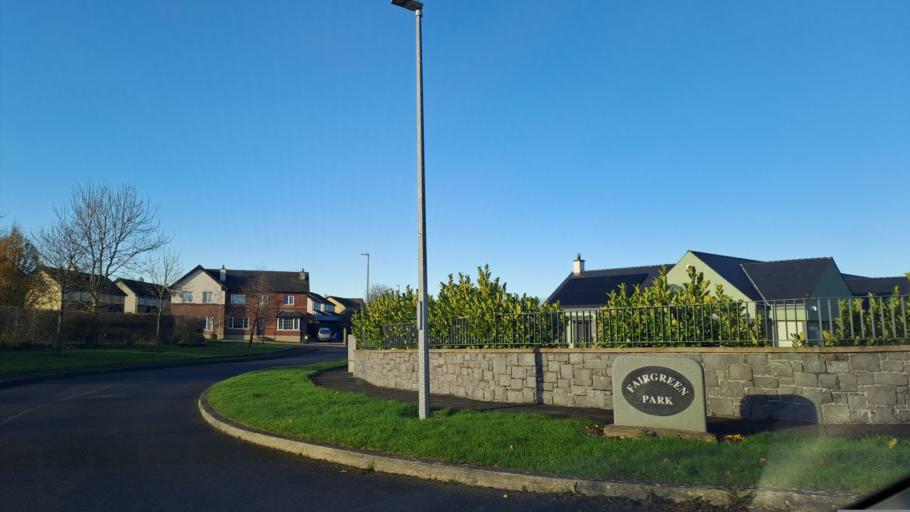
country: IE
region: Ulster
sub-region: An Cabhan
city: Mullagh
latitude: 53.8130
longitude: -6.9438
